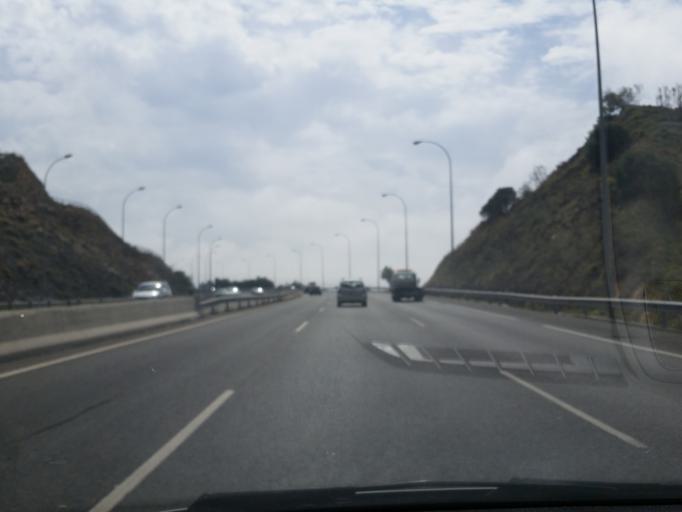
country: ES
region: Andalusia
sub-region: Provincia de Malaga
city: Malaga
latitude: 36.7537
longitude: -4.4158
